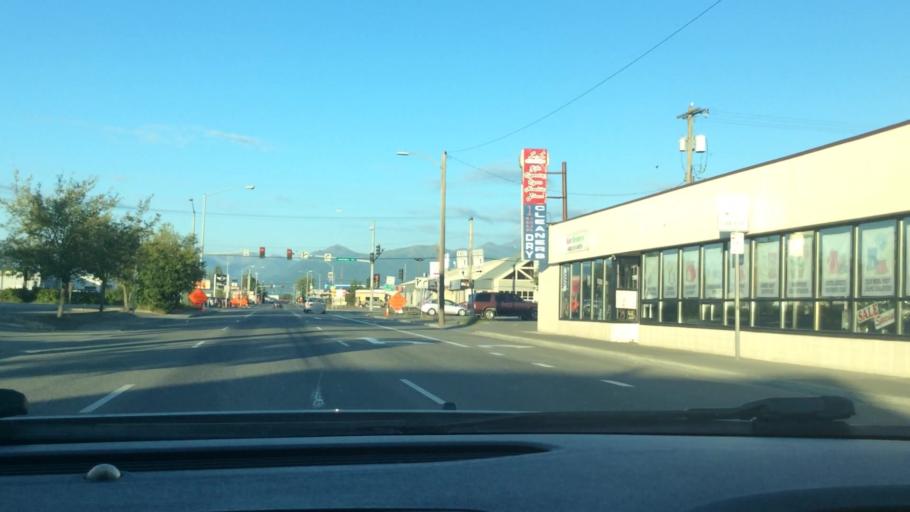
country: US
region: Alaska
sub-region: Anchorage Municipality
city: Anchorage
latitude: 61.2166
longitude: -149.8729
